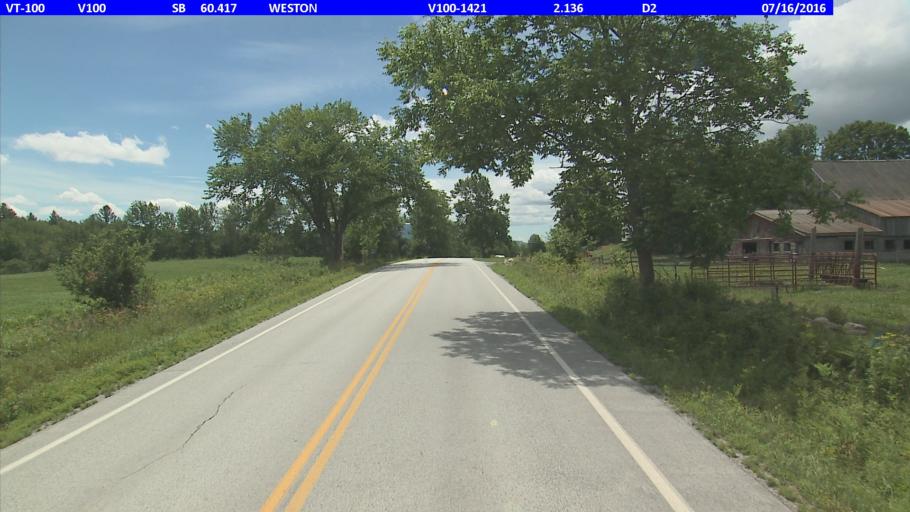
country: US
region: Vermont
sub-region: Windsor County
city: Chester
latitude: 43.2772
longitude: -72.7895
